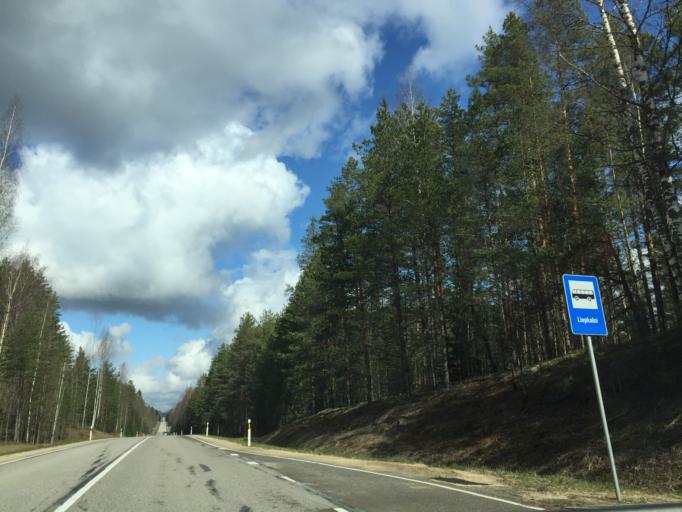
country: LV
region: Apes Novads
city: Ape
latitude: 57.4966
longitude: 26.7937
